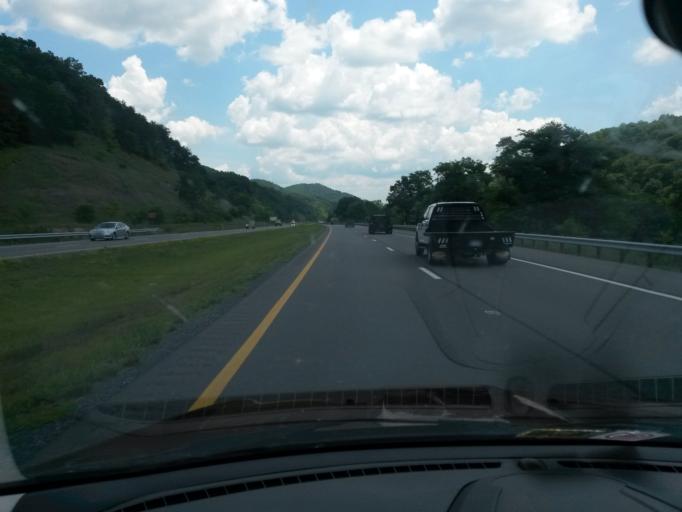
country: US
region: Virginia
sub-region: Giles County
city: Narrows
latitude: 37.3507
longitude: -80.9127
